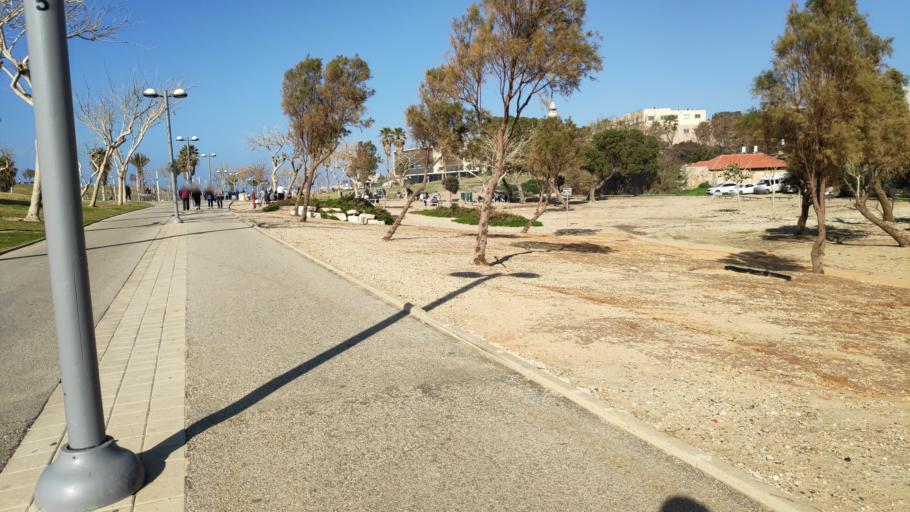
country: IL
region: Tel Aviv
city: Yafo
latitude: 32.0453
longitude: 34.7468
